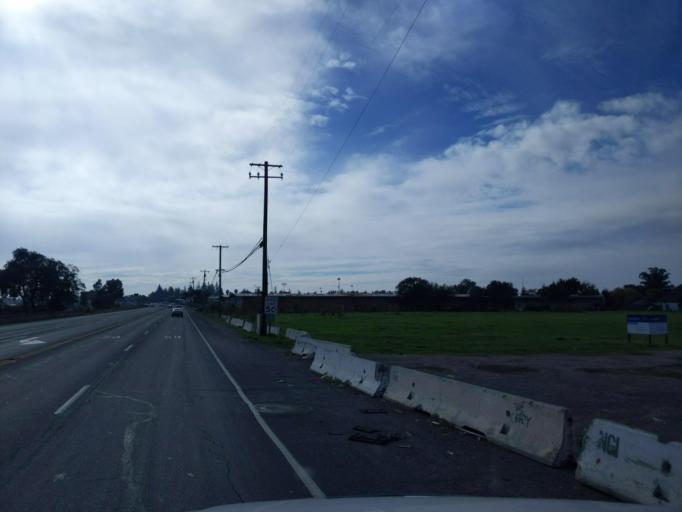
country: US
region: California
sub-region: San Joaquin County
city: August
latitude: 38.0002
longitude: -121.2605
